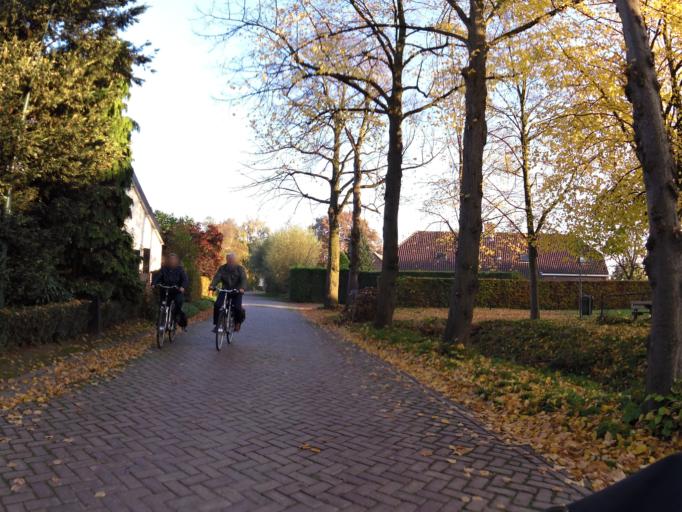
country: NL
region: Gelderland
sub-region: Gemeente Zaltbommel
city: Nederhemert-Noord
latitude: 51.7338
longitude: 5.1856
